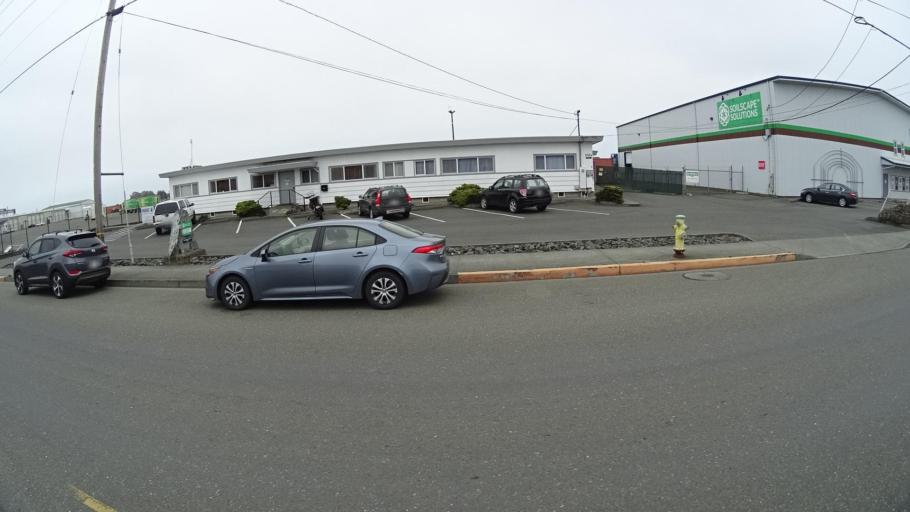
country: US
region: California
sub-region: Humboldt County
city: Eureka
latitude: 40.7975
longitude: -124.1827
